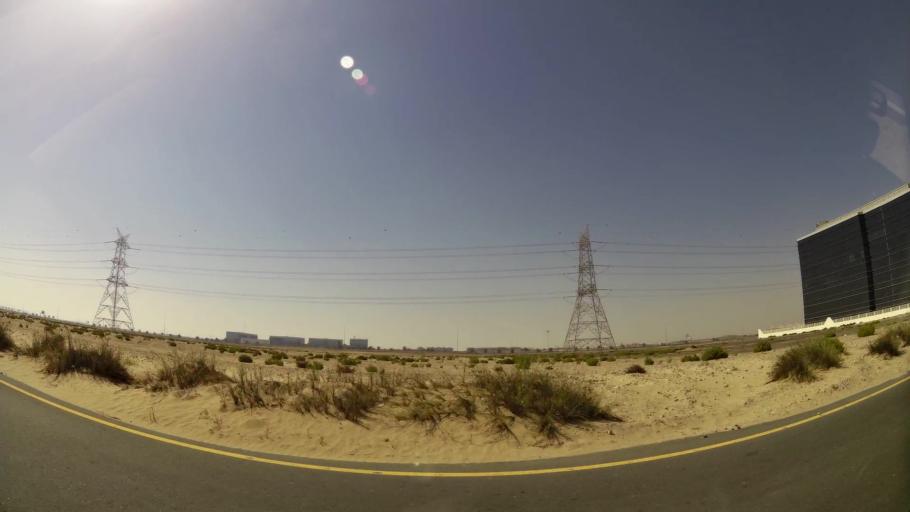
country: AE
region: Dubai
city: Dubai
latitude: 24.8991
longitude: 55.0625
